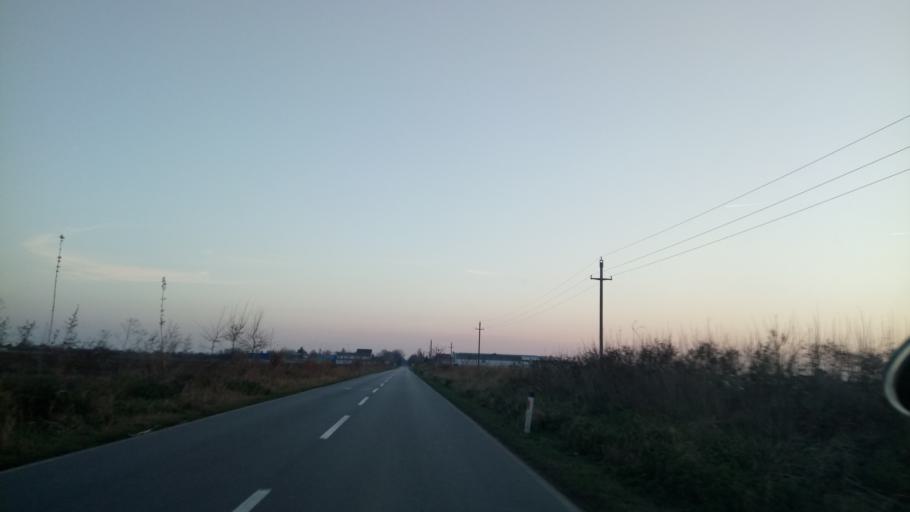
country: RS
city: Belegis
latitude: 45.0326
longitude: 20.3345
